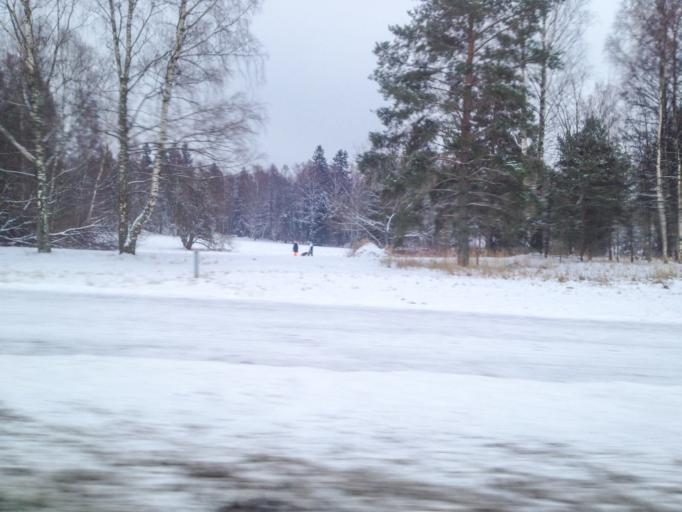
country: FI
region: Uusimaa
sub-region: Helsinki
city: Vantaa
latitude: 60.2090
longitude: 25.1604
